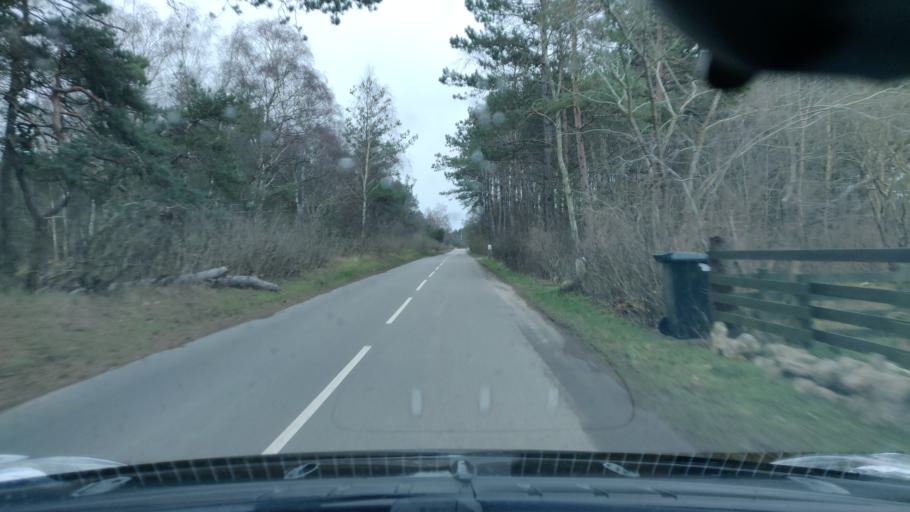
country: DK
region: Zealand
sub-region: Odsherred Kommune
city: Hojby
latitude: 55.8853
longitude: 11.5451
